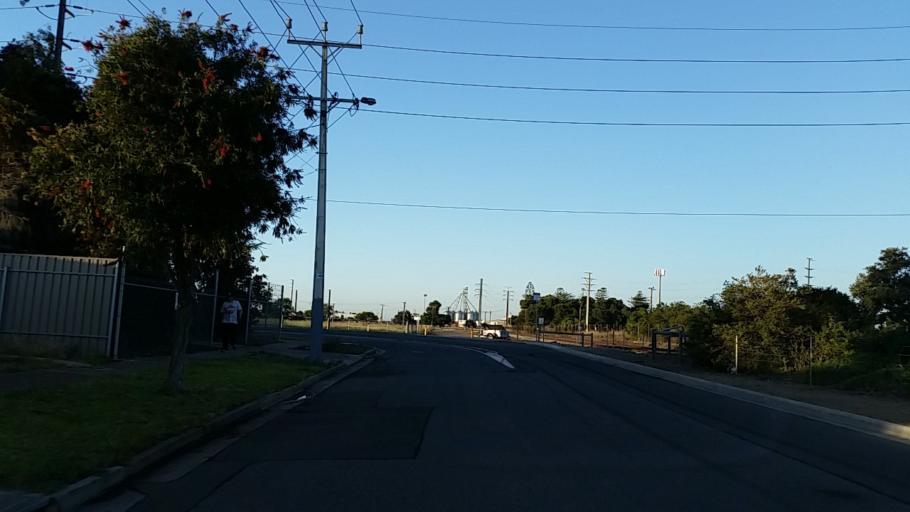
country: AU
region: South Australia
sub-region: Port Adelaide Enfield
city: Birkenhead
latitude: -34.7967
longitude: 138.5048
